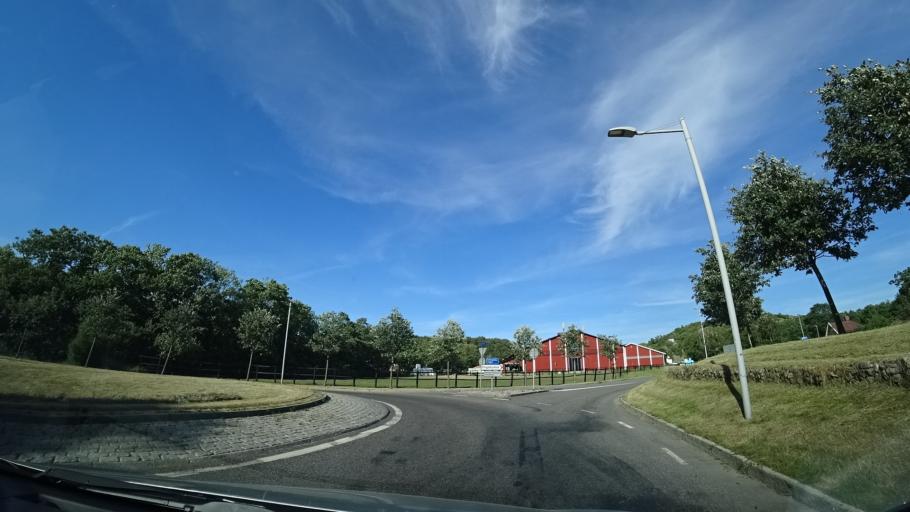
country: SE
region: Vaestra Goetaland
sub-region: Goteborg
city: Billdal
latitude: 57.5794
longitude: 11.9422
